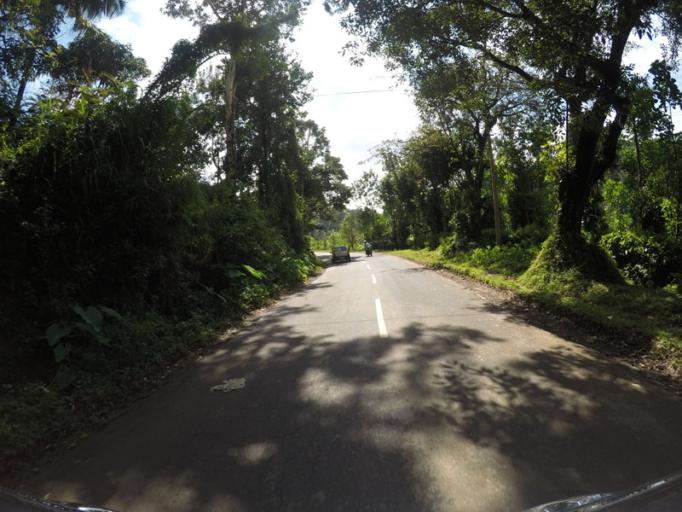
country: IN
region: Karnataka
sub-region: Kodagu
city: Suntikoppa
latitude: 12.4748
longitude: 75.7866
